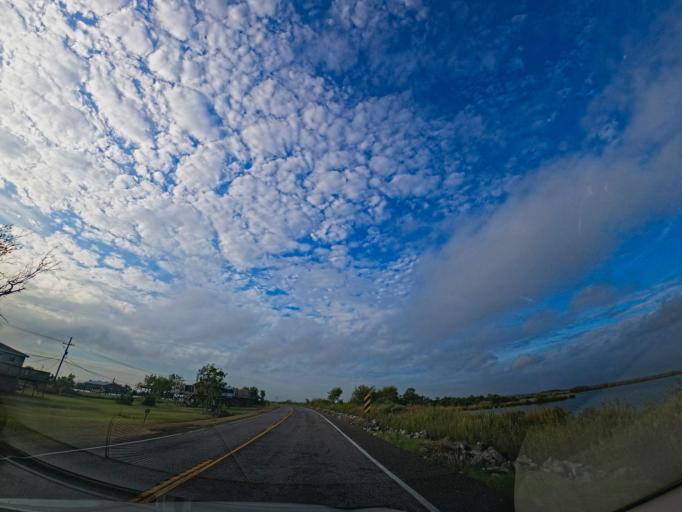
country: US
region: Louisiana
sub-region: Terrebonne Parish
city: Chauvin
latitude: 29.3666
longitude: -90.6256
